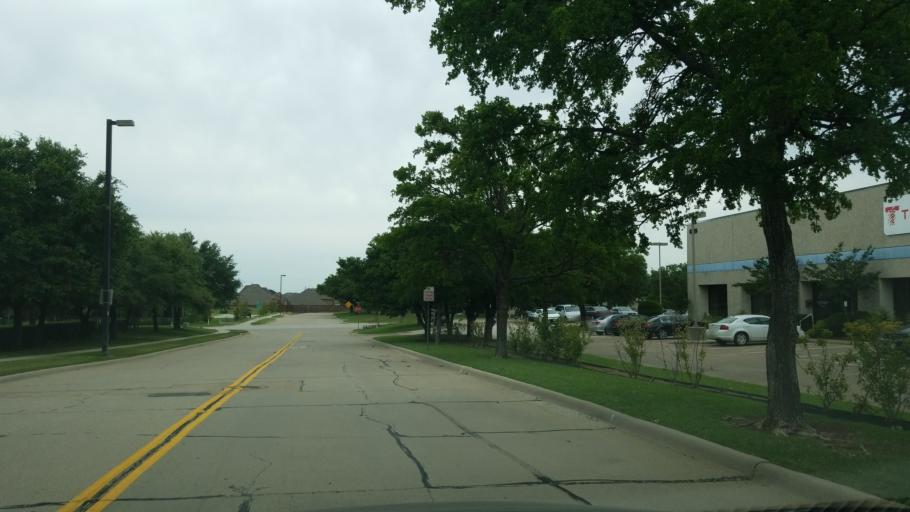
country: US
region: Texas
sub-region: Dallas County
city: Coppell
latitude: 32.8965
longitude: -96.9893
